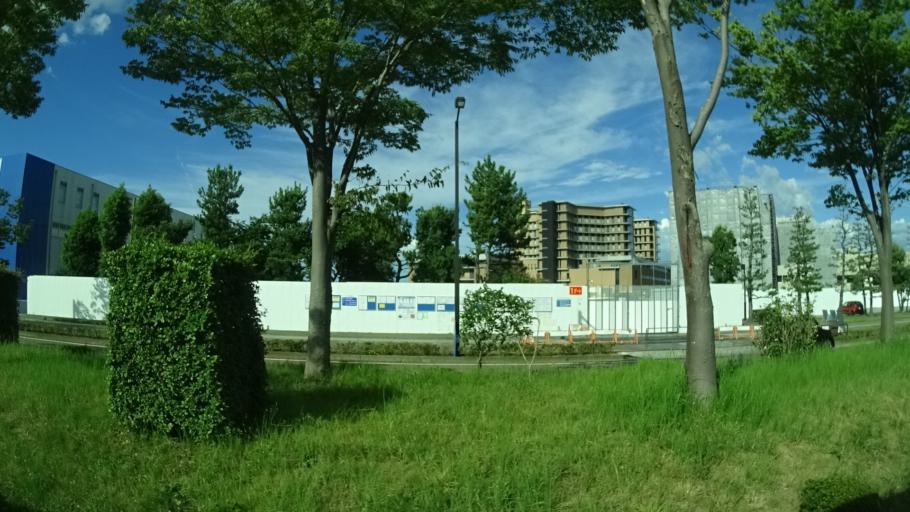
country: JP
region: Ishikawa
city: Kanazawa-shi
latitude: 36.5953
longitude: 136.6269
